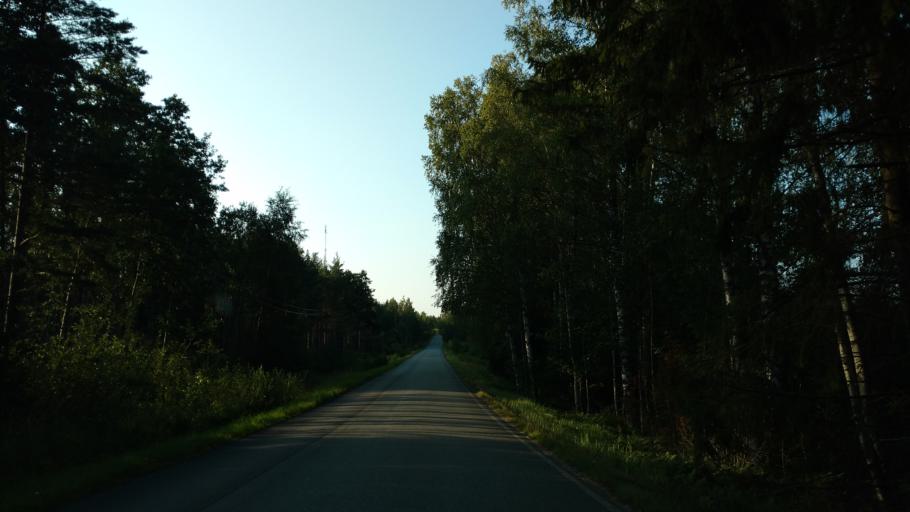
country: FI
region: Varsinais-Suomi
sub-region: Aboland-Turunmaa
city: Dragsfjaerd
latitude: 59.9411
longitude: 22.4152
